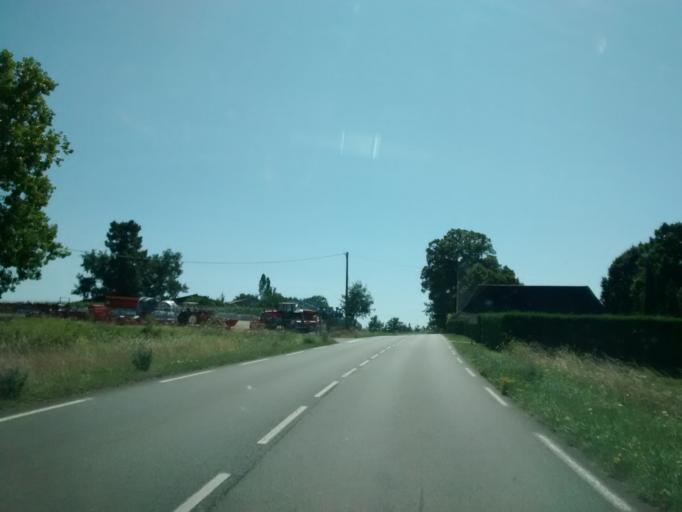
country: FR
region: Aquitaine
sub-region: Departement de la Dordogne
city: Rouffignac-Saint-Cernin-de-Reilhac
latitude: 45.0498
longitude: 0.8591
